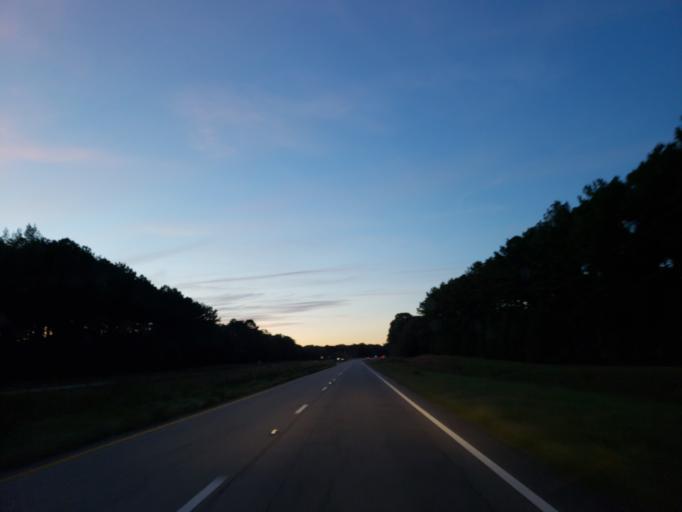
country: US
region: Mississippi
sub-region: Wayne County
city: Waynesboro
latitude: 31.8452
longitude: -88.7119
